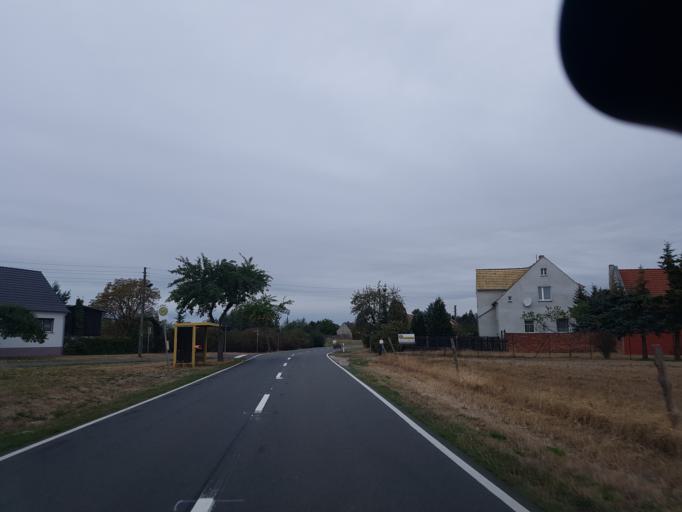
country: DE
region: Saxony-Anhalt
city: Prettin
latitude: 51.6550
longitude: 12.9426
